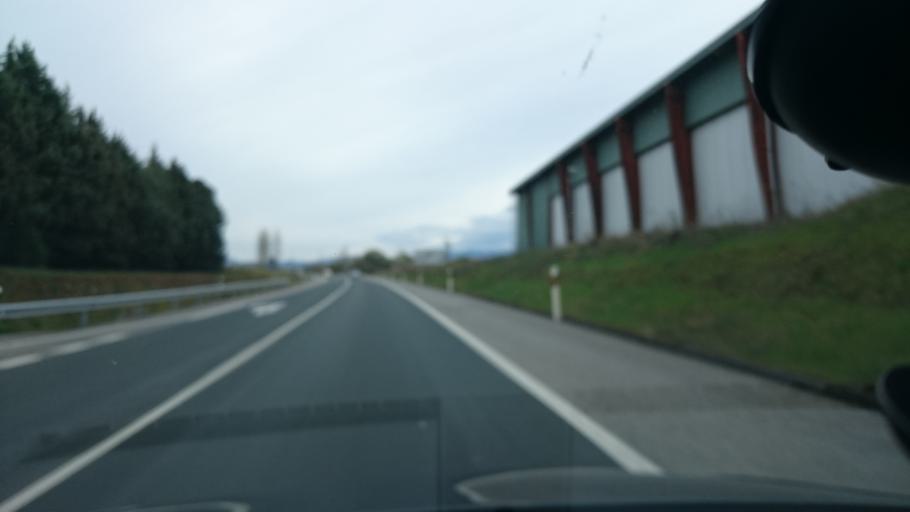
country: ES
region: Castille and Leon
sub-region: Provincia de Leon
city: Carracedelo
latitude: 42.5642
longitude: -6.7285
